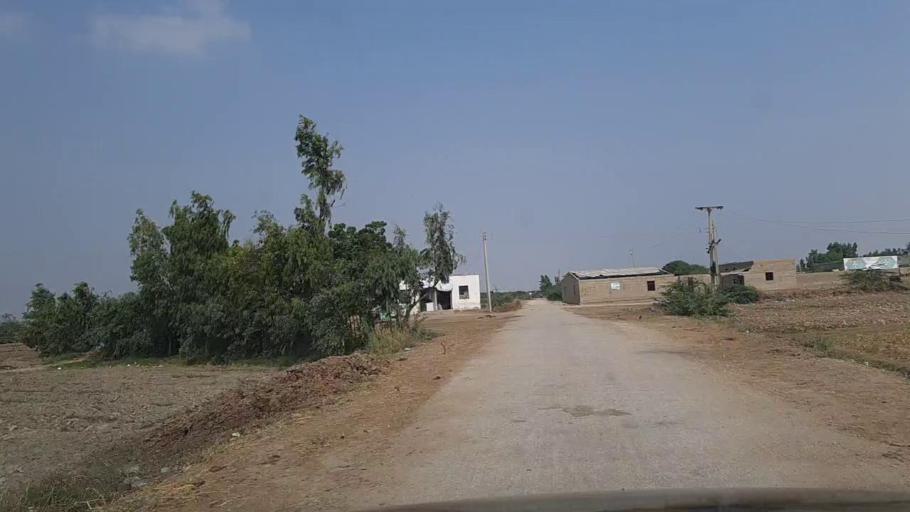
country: PK
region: Sindh
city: Thatta
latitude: 24.7976
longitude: 67.8756
